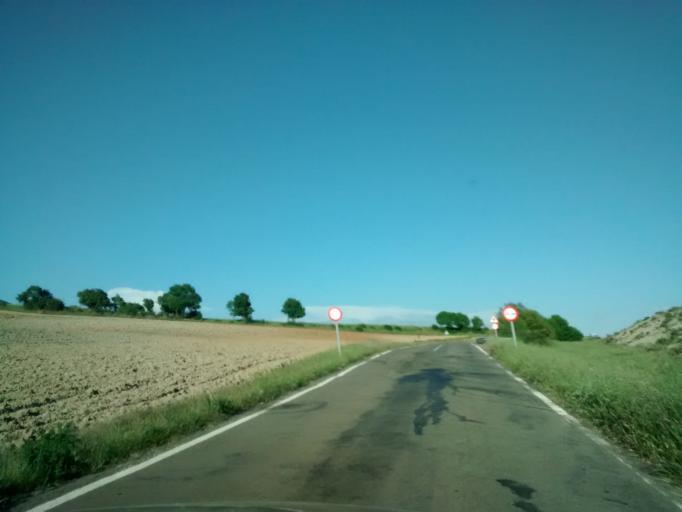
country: ES
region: Aragon
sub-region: Provincia de Huesca
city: Jaca
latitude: 42.5808
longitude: -0.5796
